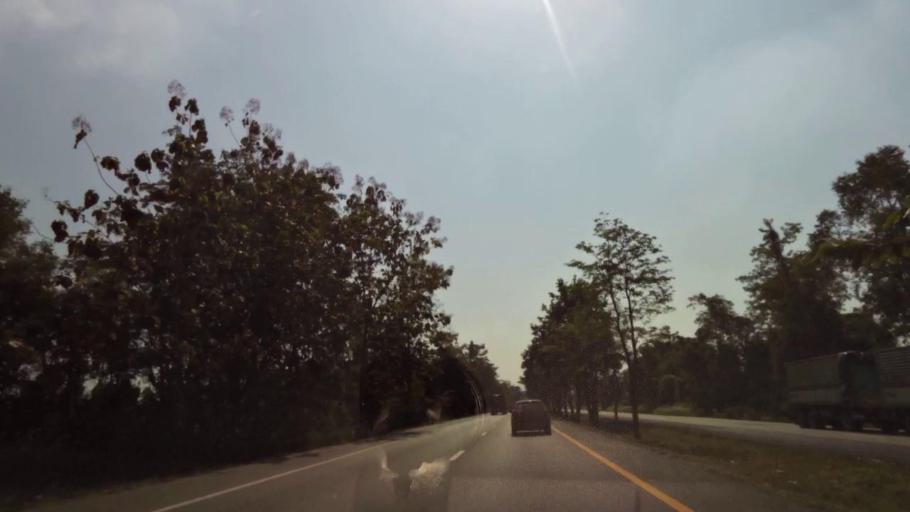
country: TH
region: Phichit
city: Bueng Na Rang
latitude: 16.0533
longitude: 100.1214
